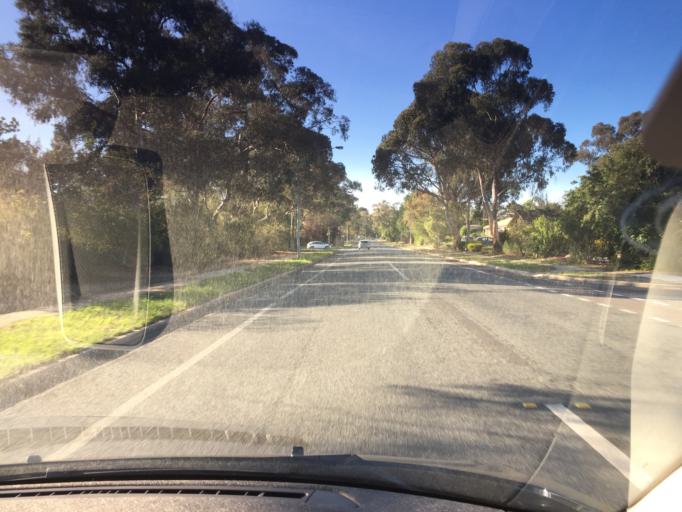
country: AU
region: Australian Capital Territory
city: Kaleen
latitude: -35.2256
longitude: 149.1111
